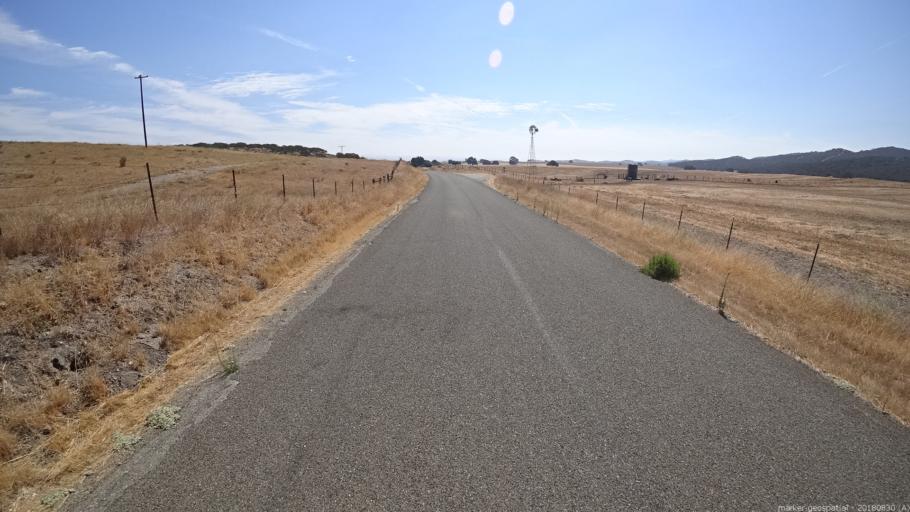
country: US
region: California
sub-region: Monterey County
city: King City
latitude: 36.1132
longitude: -121.1066
